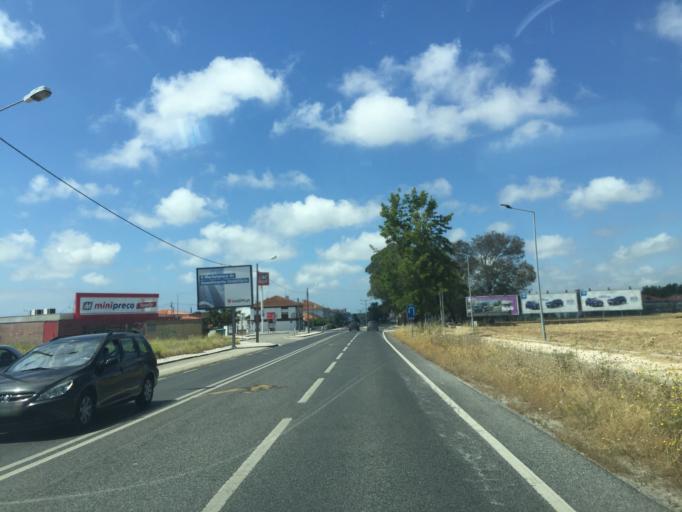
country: PT
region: Leiria
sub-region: Marinha Grande
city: Marinha Grande
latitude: 39.7383
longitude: -8.9337
